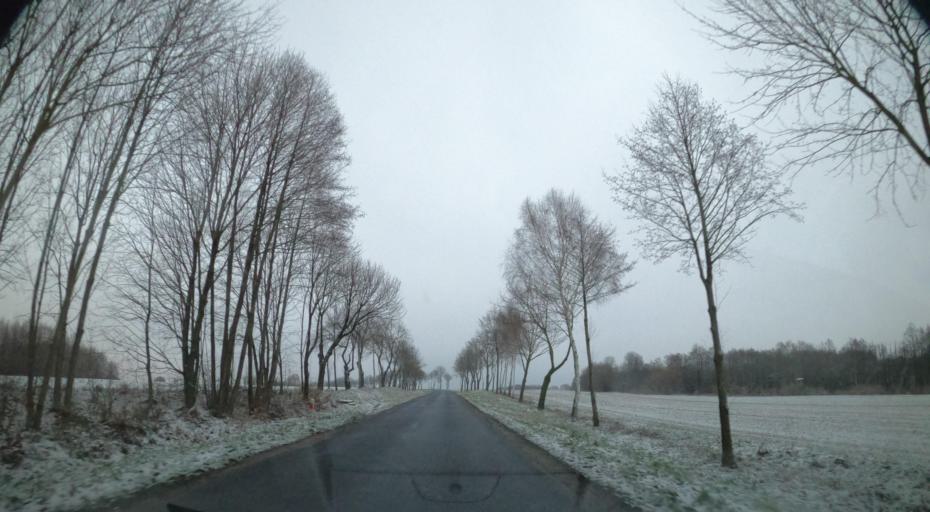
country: PL
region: Kujawsko-Pomorskie
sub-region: Powiat lipnowski
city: Wielgie
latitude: 52.7021
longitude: 19.2869
